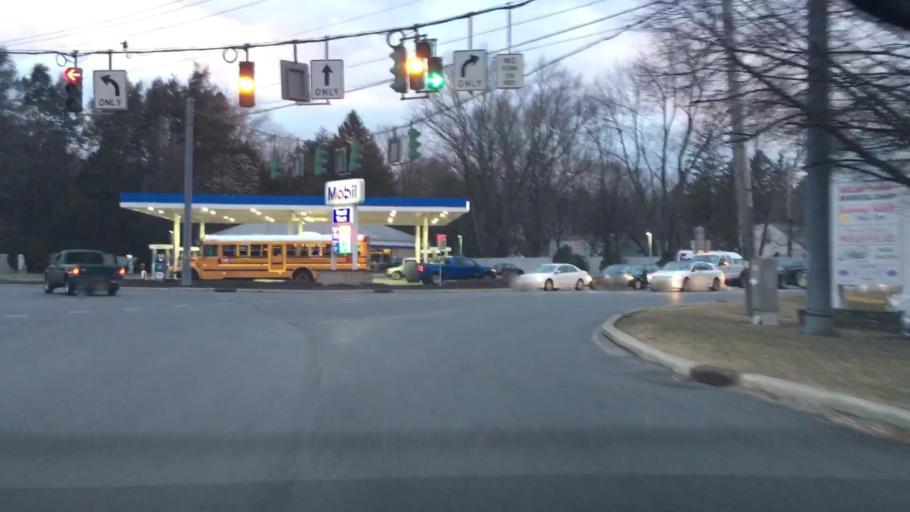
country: US
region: New York
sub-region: Dutchess County
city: Red Oaks Mill
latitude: 41.6555
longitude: -73.8744
